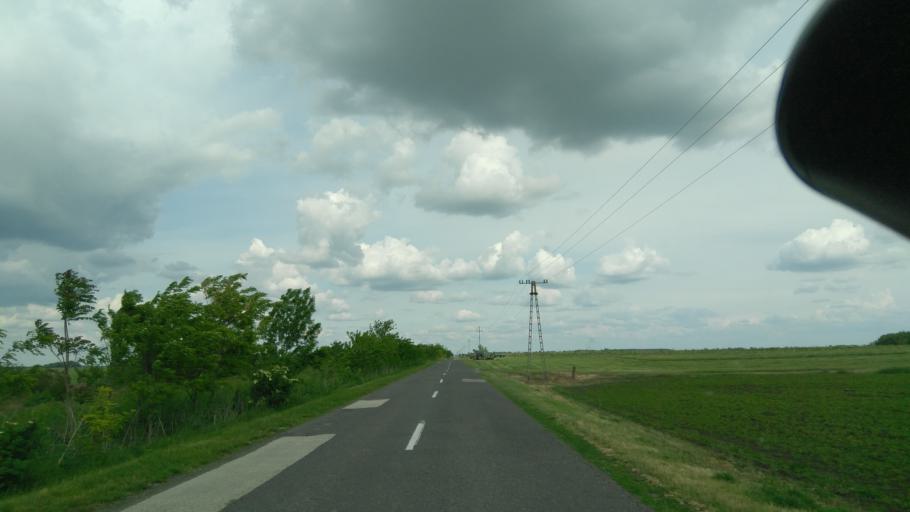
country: HU
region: Bekes
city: Mezohegyes
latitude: 46.3114
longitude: 20.8595
